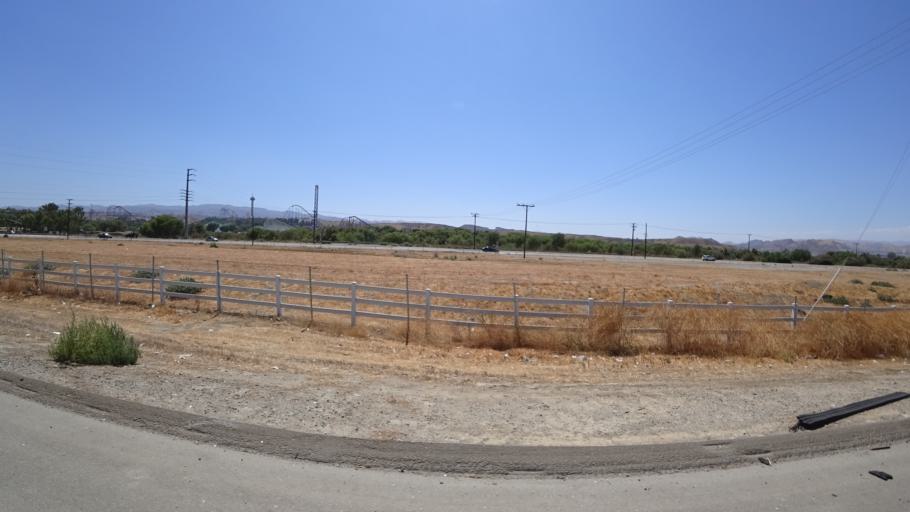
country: US
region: California
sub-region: Los Angeles County
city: Valencia
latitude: 34.4350
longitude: -118.5931
